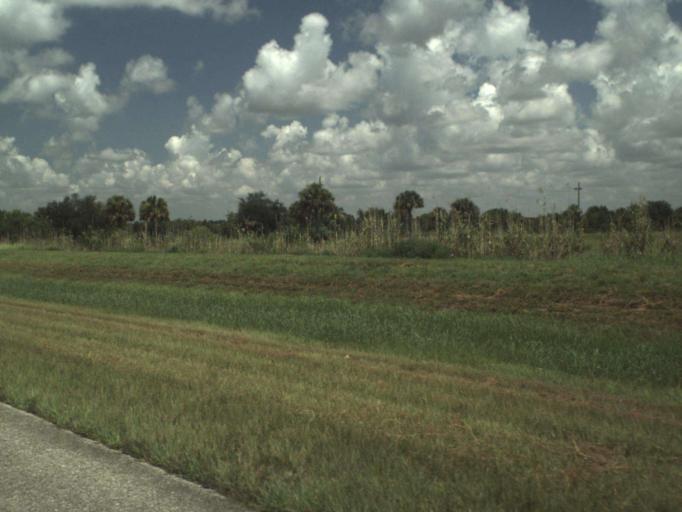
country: US
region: Florida
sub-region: Indian River County
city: West Vero Corridor
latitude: 27.6401
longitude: -80.5930
